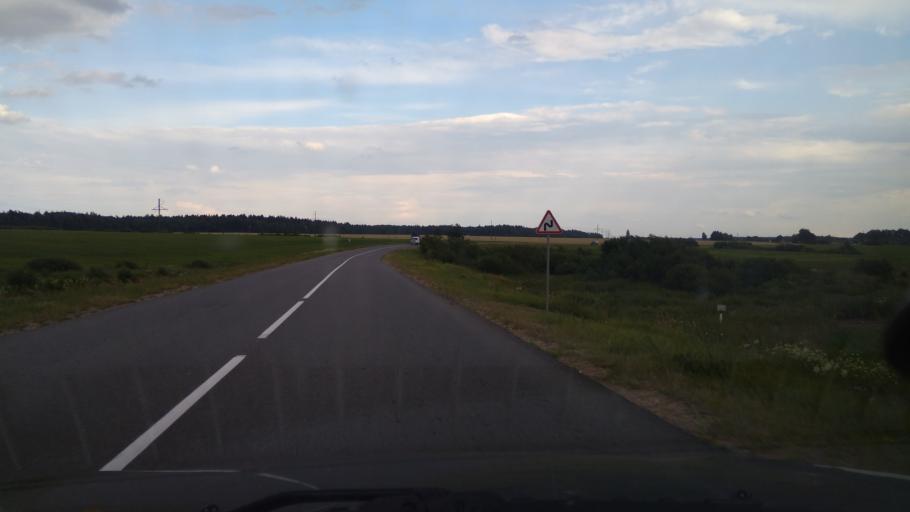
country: BY
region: Minsk
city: Il'ya
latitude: 54.4224
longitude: 27.2397
